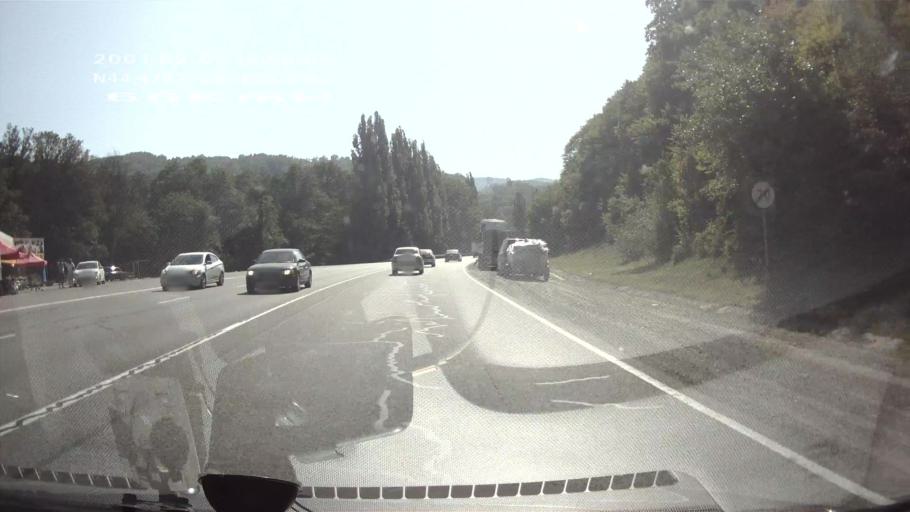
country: RU
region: Krasnodarskiy
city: Novomikhaylovskiy
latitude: 44.4780
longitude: 38.9020
